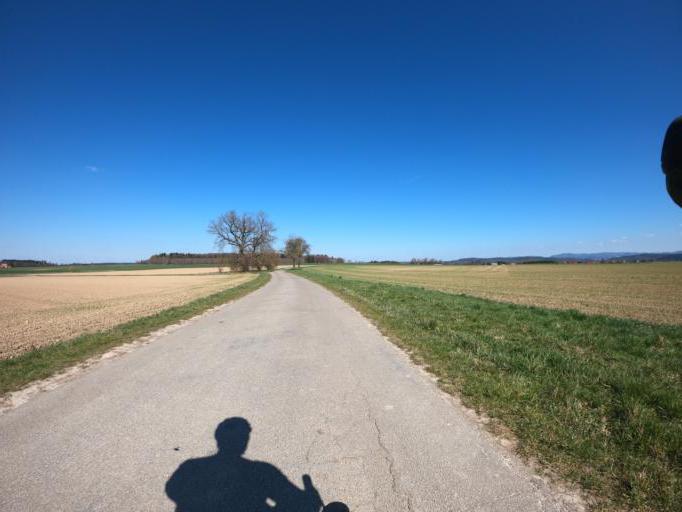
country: DE
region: Baden-Wuerttemberg
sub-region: Tuebingen Region
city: Haigerloch
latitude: 48.3893
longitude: 8.8251
